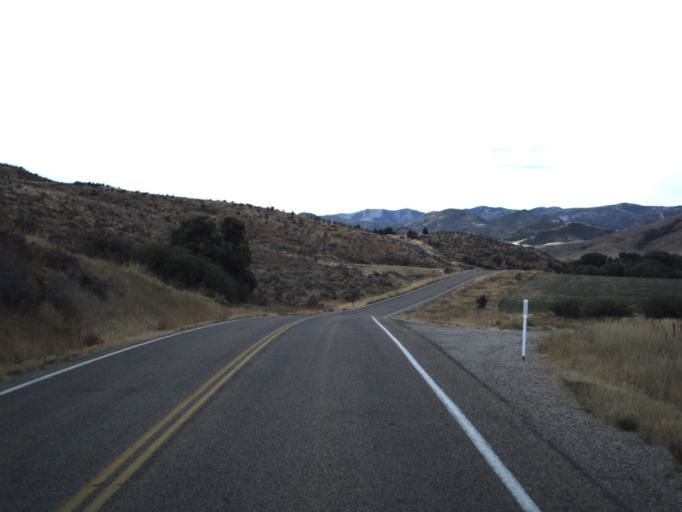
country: US
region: Utah
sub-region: Morgan County
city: Morgan
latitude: 41.0024
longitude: -111.6769
